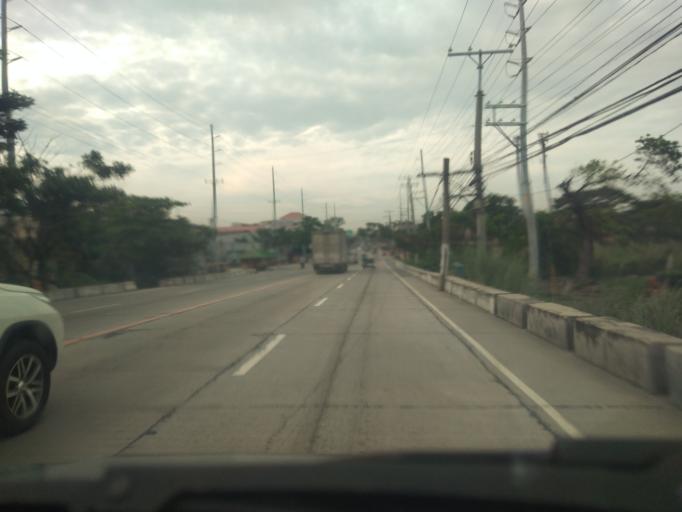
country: PH
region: Central Luzon
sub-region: Province of Pampanga
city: San Fernando
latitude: 15.0270
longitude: 120.6973
